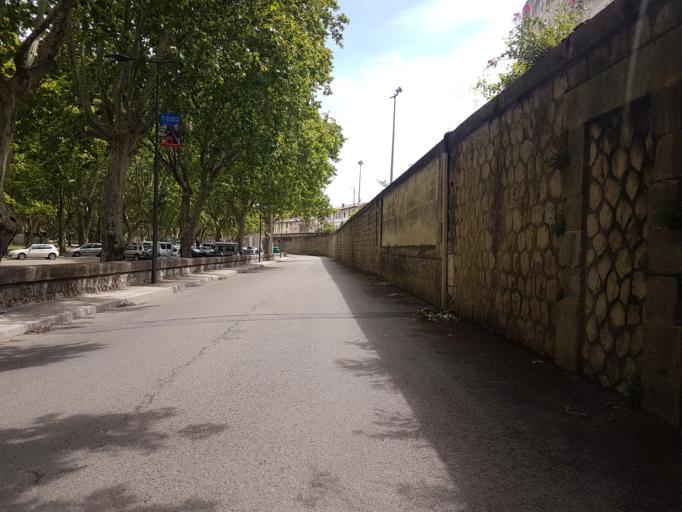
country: FR
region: Languedoc-Roussillon
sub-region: Departement du Gard
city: Beaucaire
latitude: 43.8109
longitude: 4.6449
